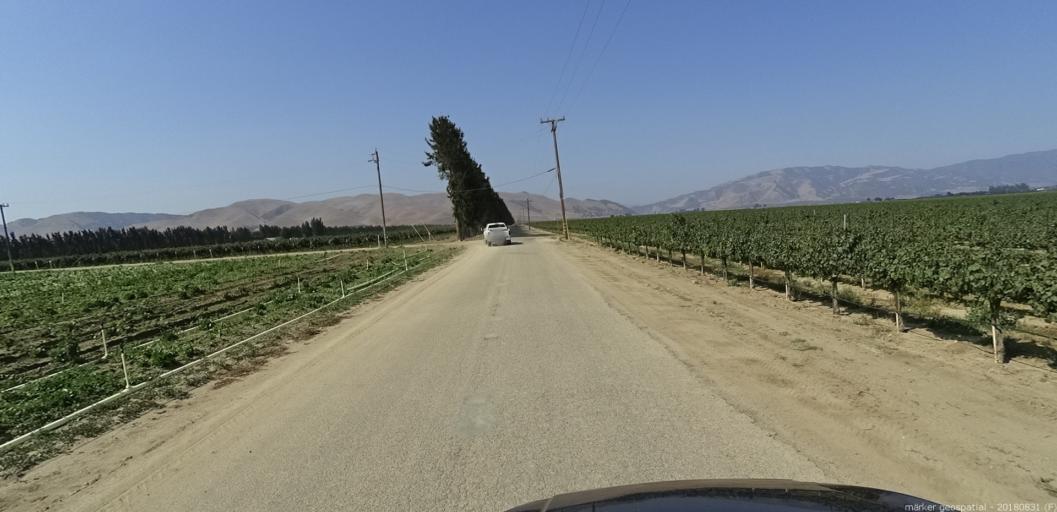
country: US
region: California
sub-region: Monterey County
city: Greenfield
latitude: 36.3056
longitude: -121.2348
